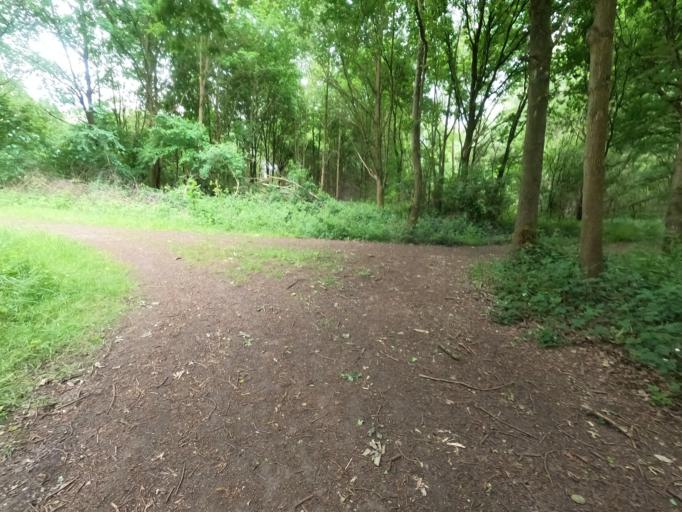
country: BE
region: Flanders
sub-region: Provincie Vlaams-Brabant
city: Tremelo
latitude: 50.9846
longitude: 4.7168
